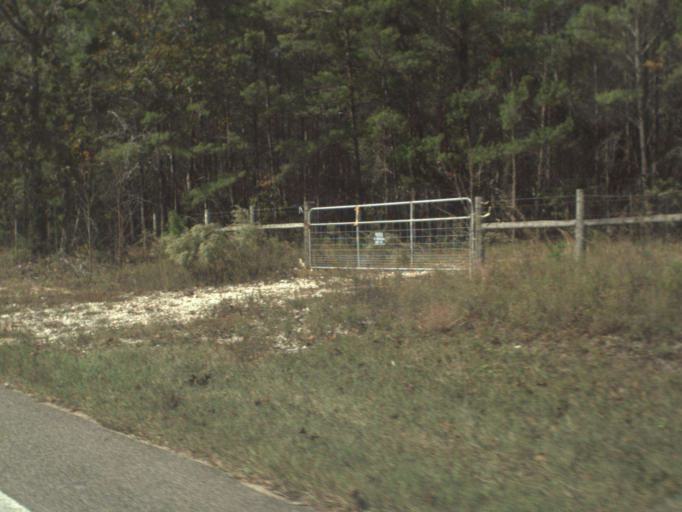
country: US
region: Florida
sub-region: Liberty County
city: Bristol
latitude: 30.4840
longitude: -84.9141
